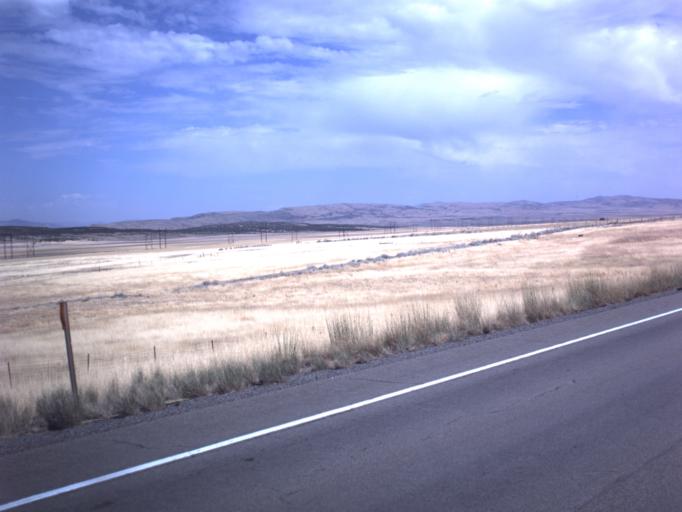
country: US
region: Utah
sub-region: Sanpete County
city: Gunnison
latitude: 39.4191
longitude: -111.9225
